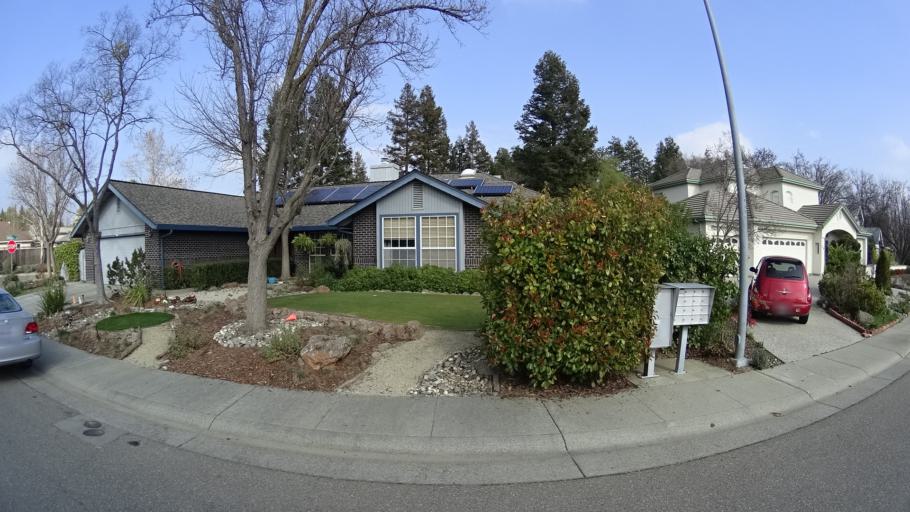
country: US
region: California
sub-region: Yolo County
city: Davis
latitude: 38.5711
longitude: -121.7566
